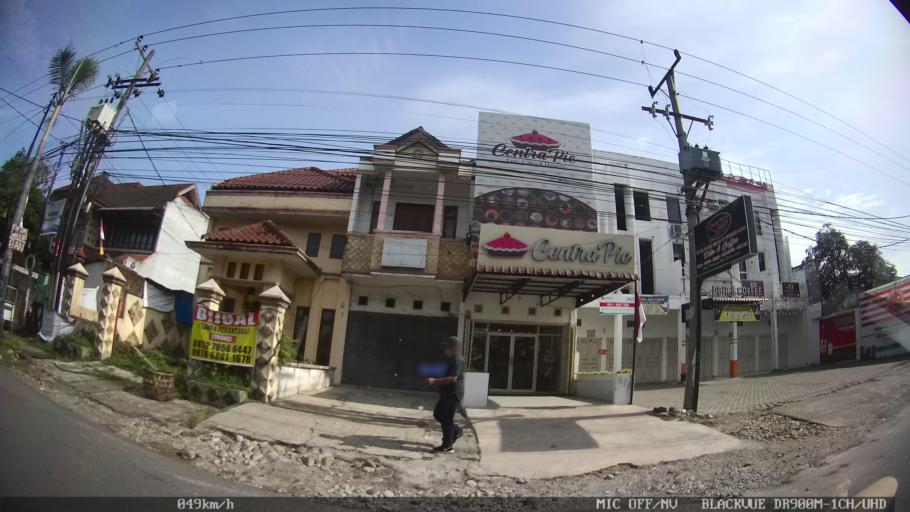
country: ID
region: North Sumatra
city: Medan
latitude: 3.5678
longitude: 98.6444
